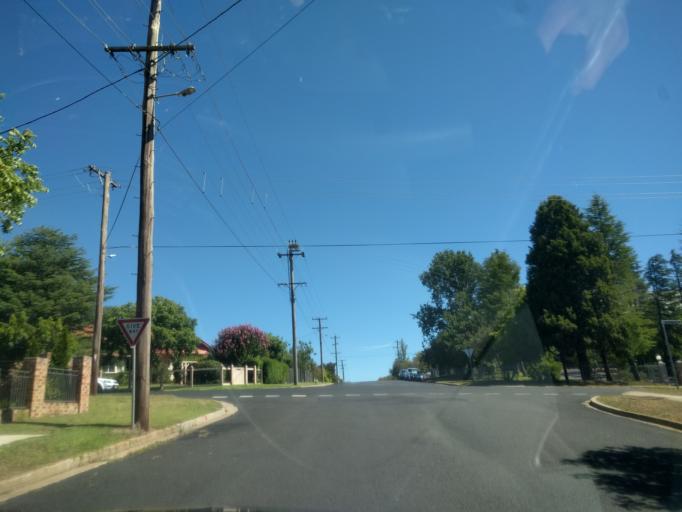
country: AU
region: New South Wales
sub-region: Armidale Dumaresq
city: Armidale
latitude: -30.5224
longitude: 151.6640
